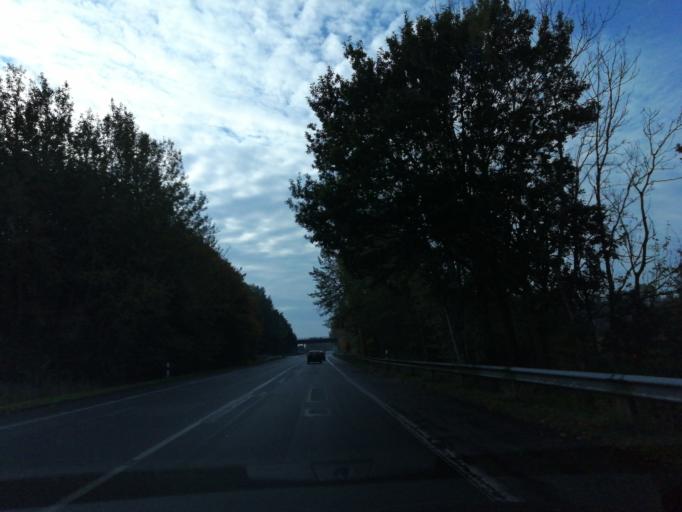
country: DE
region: Lower Saxony
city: Fedderwarden
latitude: 53.5803
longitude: 8.0567
